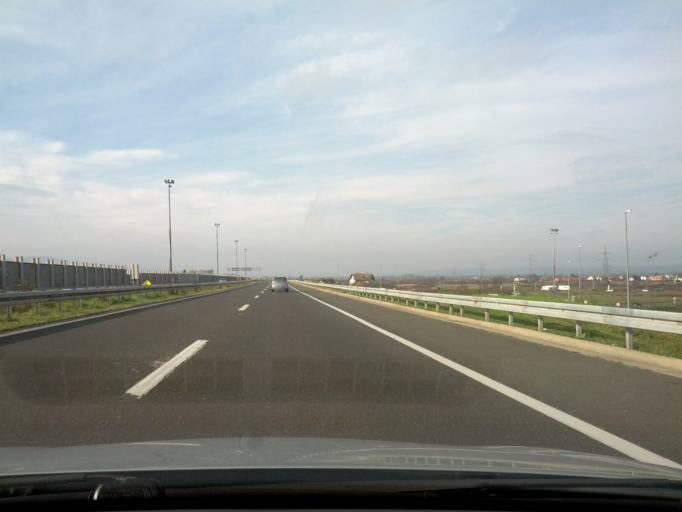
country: HR
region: Zagrebacka
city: Bestovje
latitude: 45.7971
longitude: 15.7867
